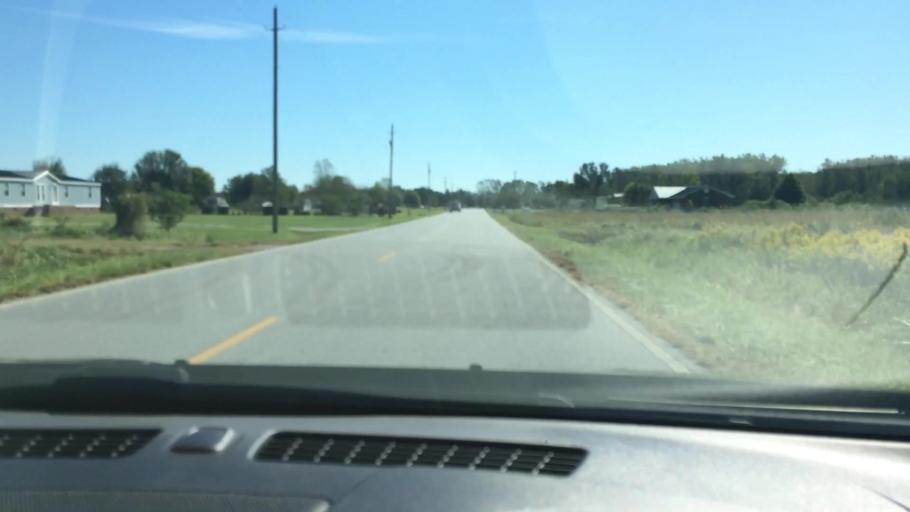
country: US
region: North Carolina
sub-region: Pitt County
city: Grifton
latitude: 35.3814
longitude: -77.3728
